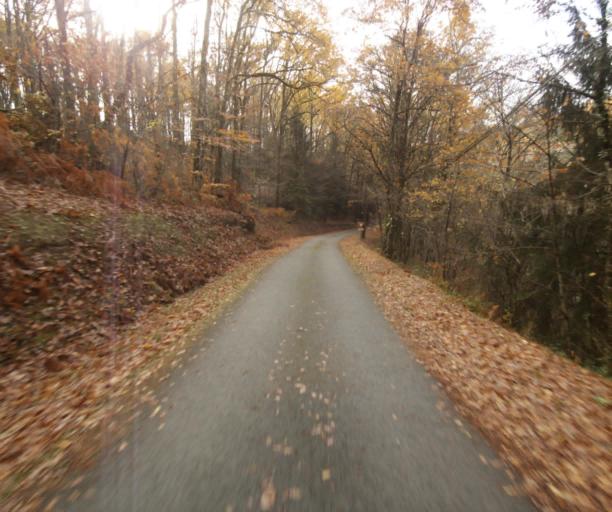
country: FR
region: Limousin
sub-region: Departement de la Correze
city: Sainte-Fereole
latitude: 45.2123
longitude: 1.6317
